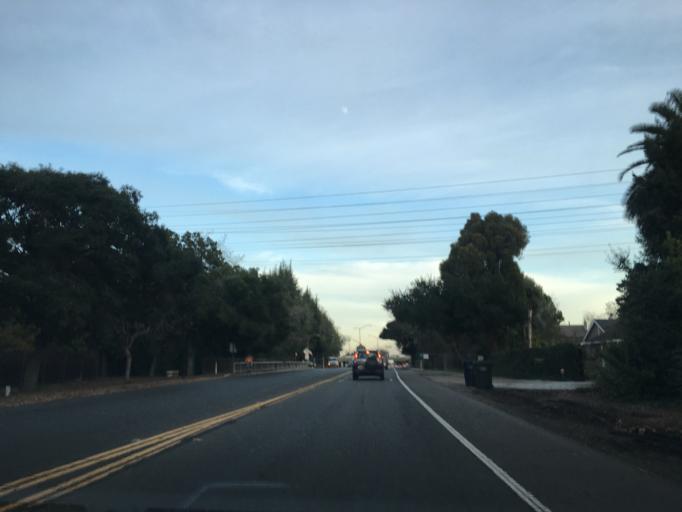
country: US
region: California
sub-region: Santa Clara County
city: Sunnyvale
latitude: 37.3521
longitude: -122.0643
